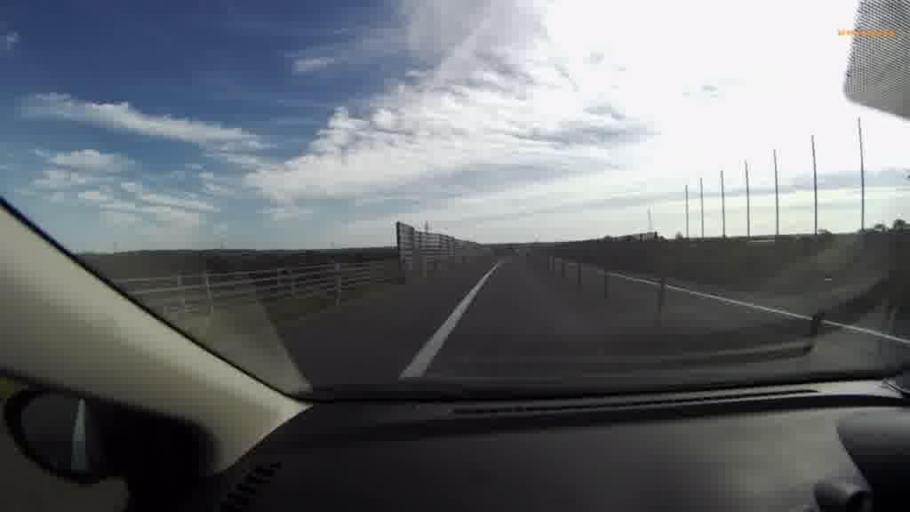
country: JP
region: Hokkaido
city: Kushiro
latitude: 43.0354
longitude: 144.3714
